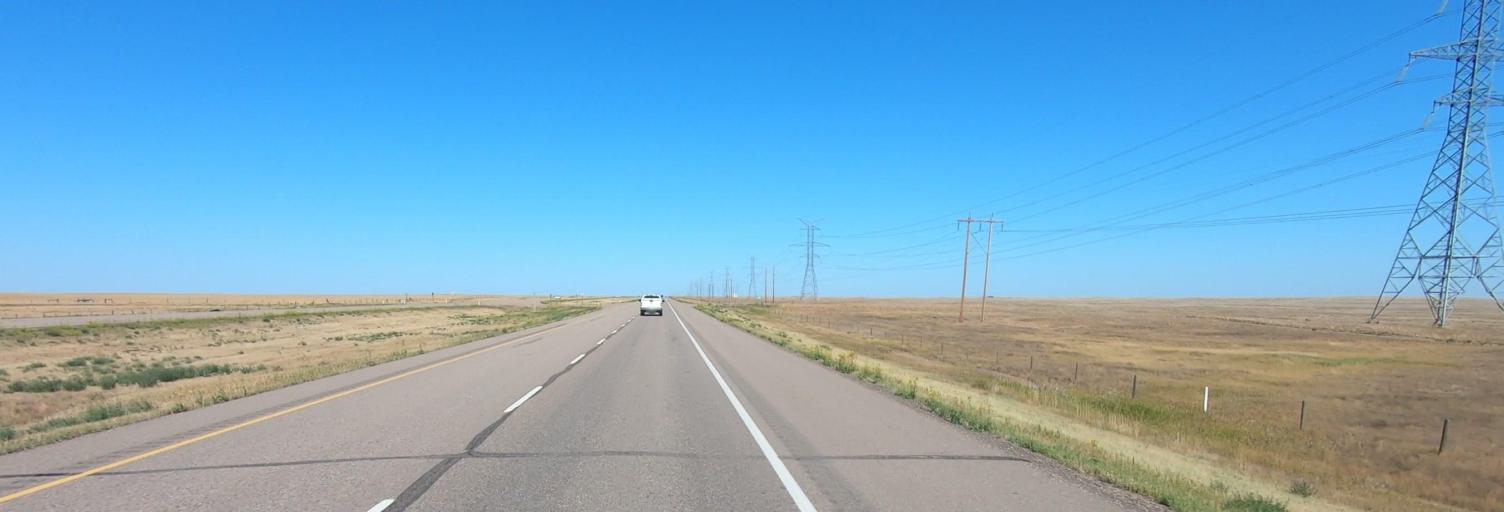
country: CA
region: Alberta
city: Bow Island
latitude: 50.2828
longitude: -111.2851
